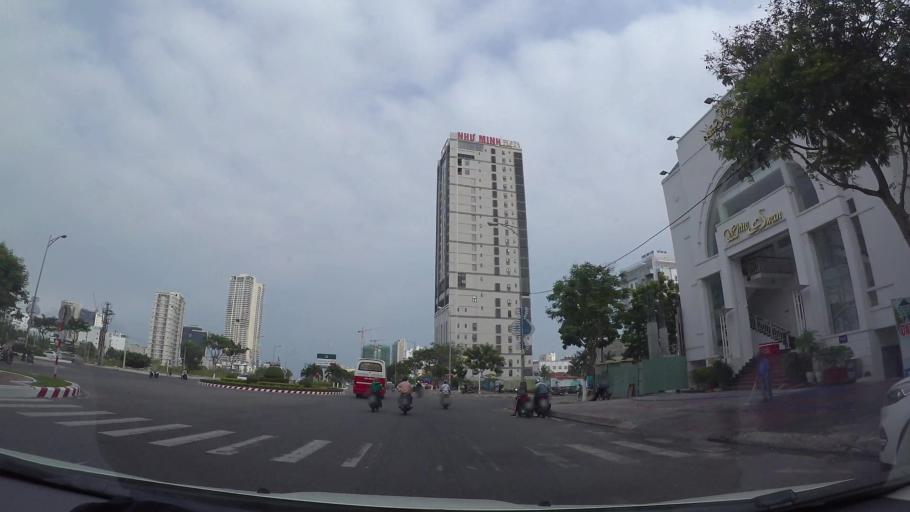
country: VN
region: Da Nang
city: Son Tra
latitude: 16.0702
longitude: 108.2375
